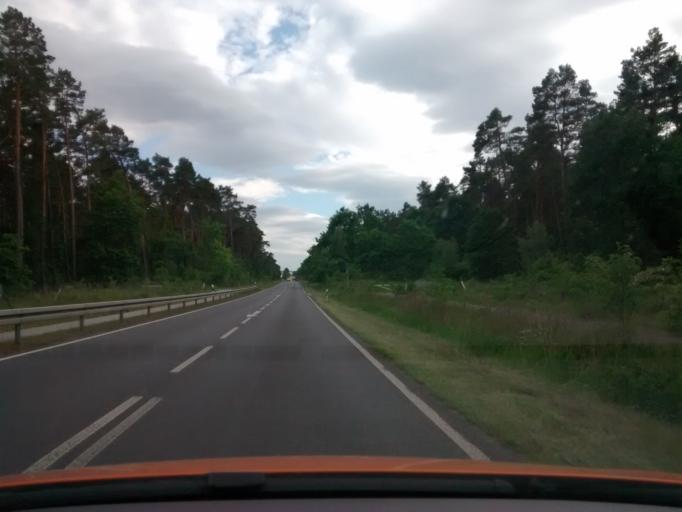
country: DE
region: Berlin
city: Bohnsdorf
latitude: 52.3830
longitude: 13.5677
